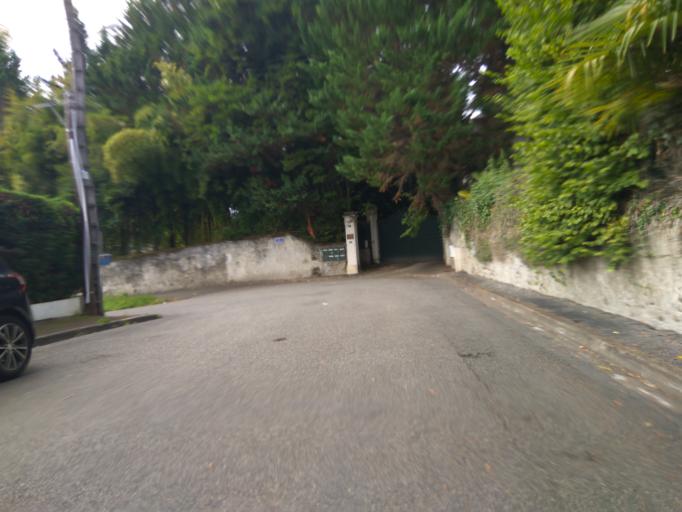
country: FR
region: Aquitaine
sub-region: Departement des Pyrenees-Atlantiques
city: Bizanos
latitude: 43.2970
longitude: -0.3450
